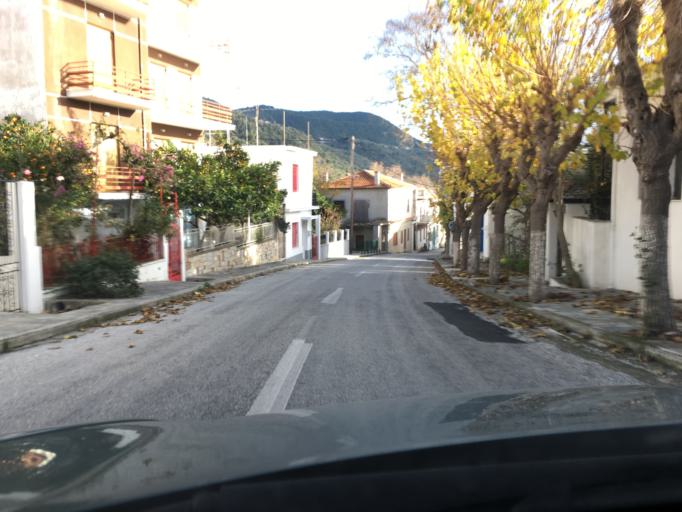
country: GR
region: Thessaly
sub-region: Nomos Magnisias
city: Skopelos
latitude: 39.1685
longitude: 23.6126
